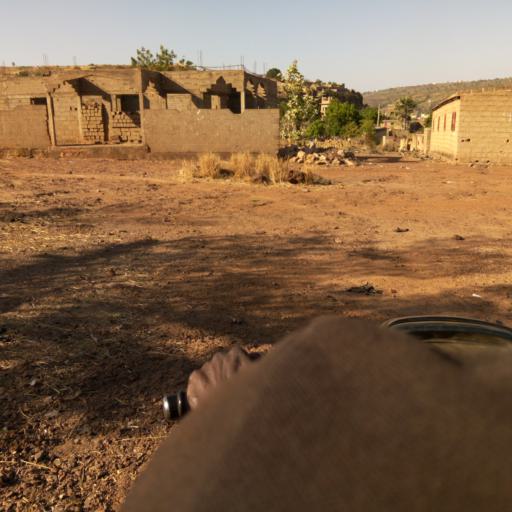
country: ML
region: Bamako
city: Bamako
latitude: 12.6555
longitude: -8.0386
